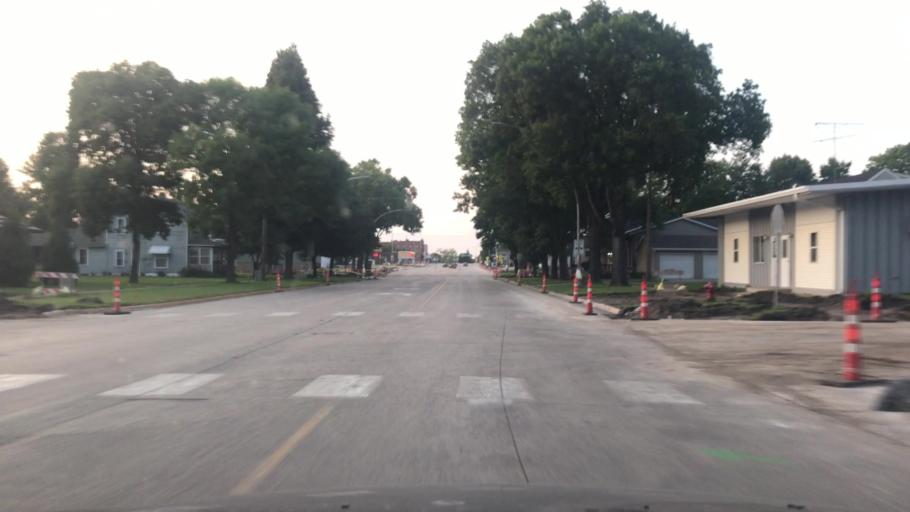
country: US
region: Minnesota
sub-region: Redwood County
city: Redwood Falls
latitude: 44.5359
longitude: -95.1195
